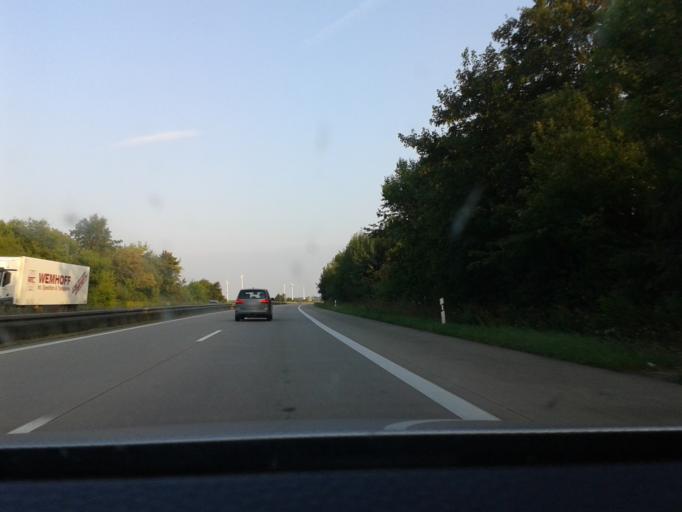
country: DE
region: Saxony
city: Dobeln
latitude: 51.1478
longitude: 13.1433
